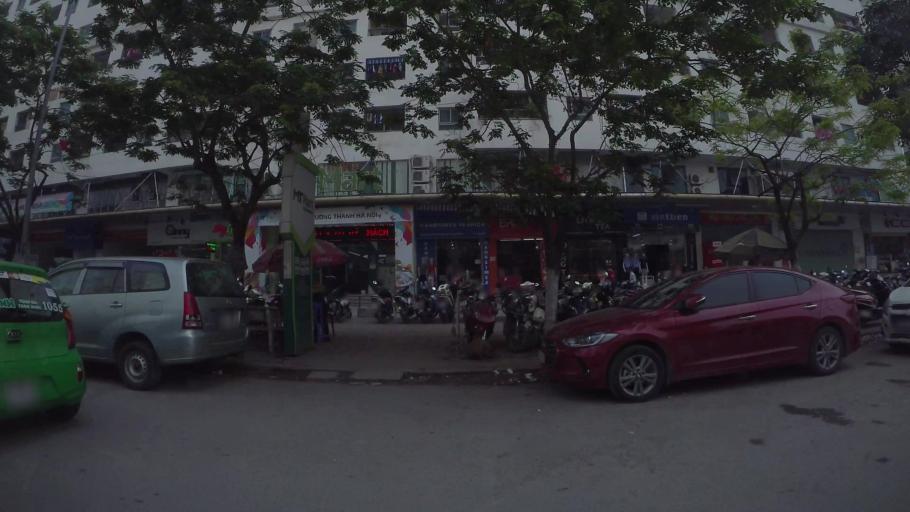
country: VN
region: Ha Noi
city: Van Dien
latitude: 20.9643
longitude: 105.8258
